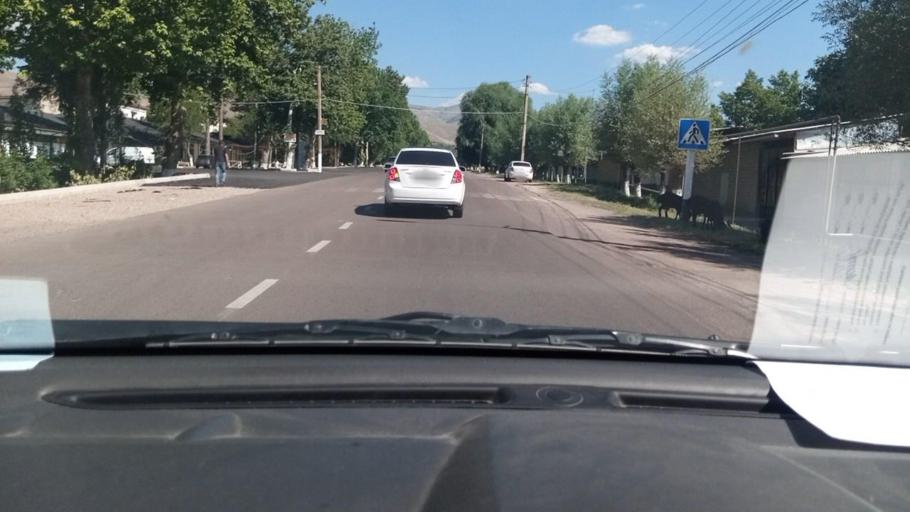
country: UZ
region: Toshkent
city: Angren
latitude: 41.0404
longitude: 70.0932
